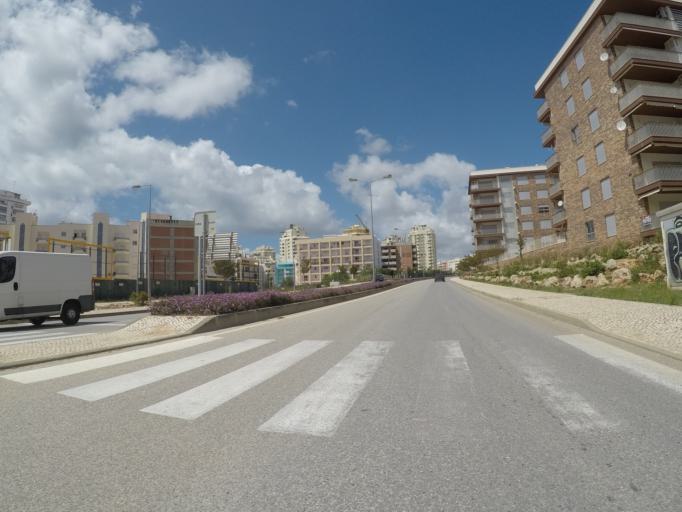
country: PT
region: Faro
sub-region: Silves
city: Armacao de Pera
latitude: 37.1043
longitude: -8.3630
